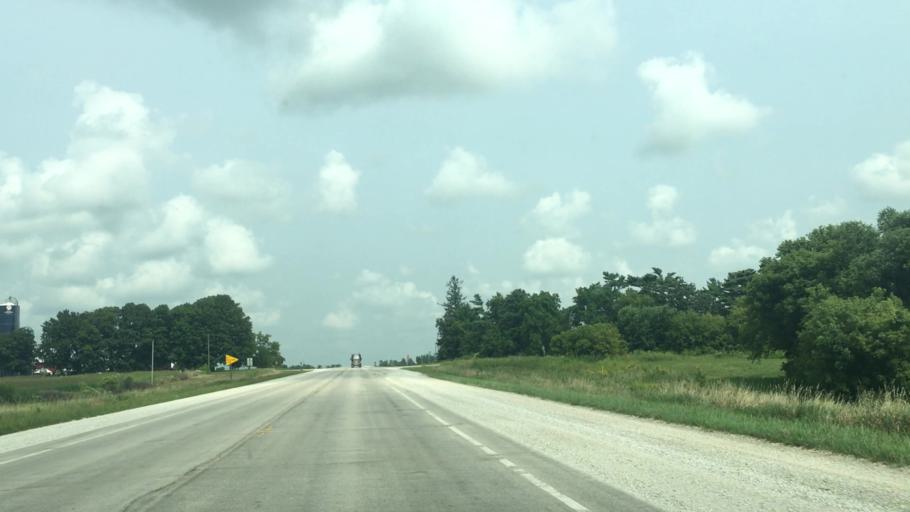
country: US
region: Minnesota
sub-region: Fillmore County
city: Harmony
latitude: 43.4706
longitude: -91.8700
